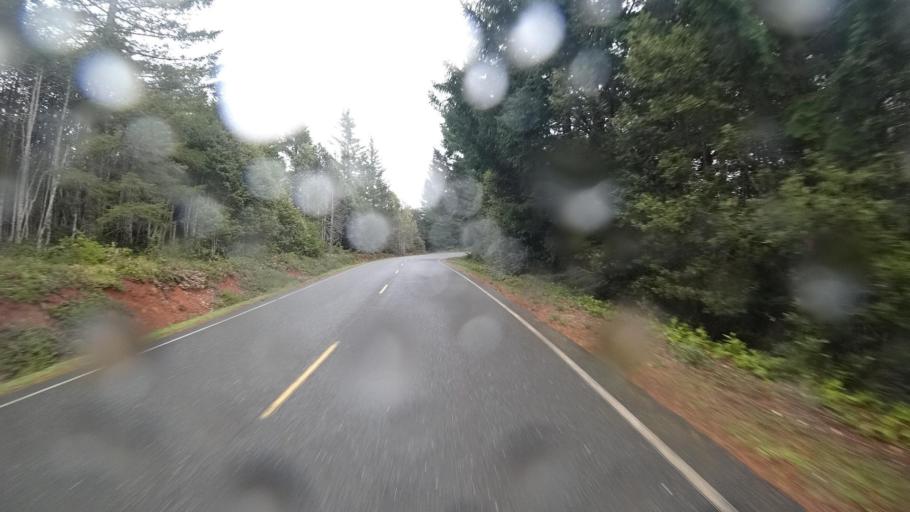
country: US
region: California
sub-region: Humboldt County
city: Willow Creek
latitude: 41.1886
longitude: -123.8162
